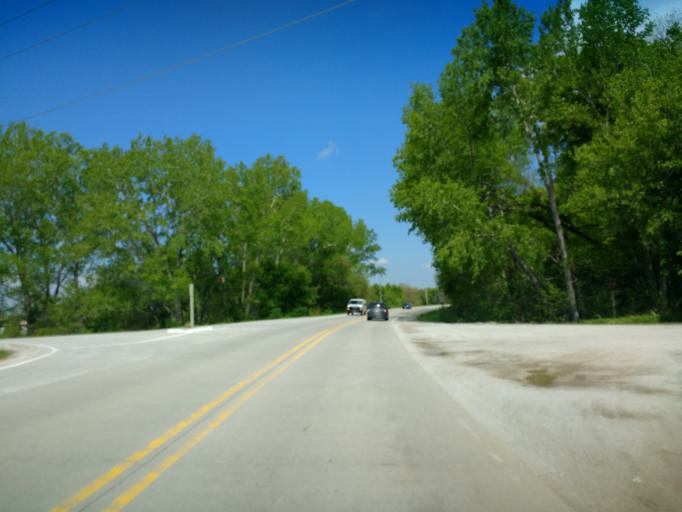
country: US
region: Iowa
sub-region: Harrison County
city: Missouri Valley
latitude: 41.4339
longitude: -95.8677
